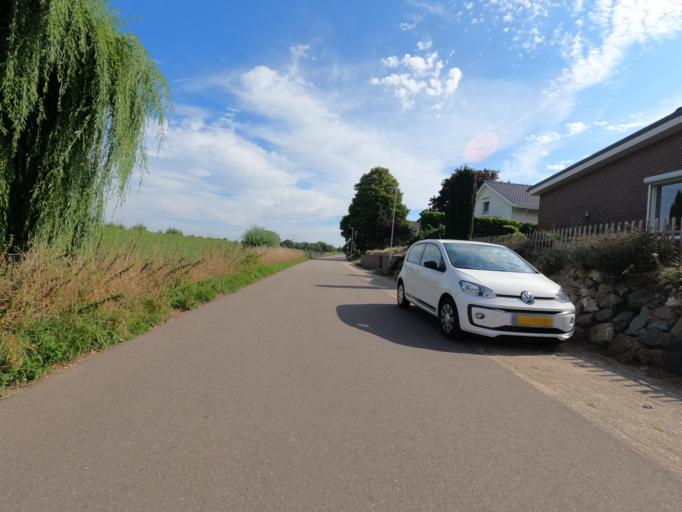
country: BE
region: Flanders
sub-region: Provincie Limburg
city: Maaseik
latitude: 51.0872
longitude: 5.8214
